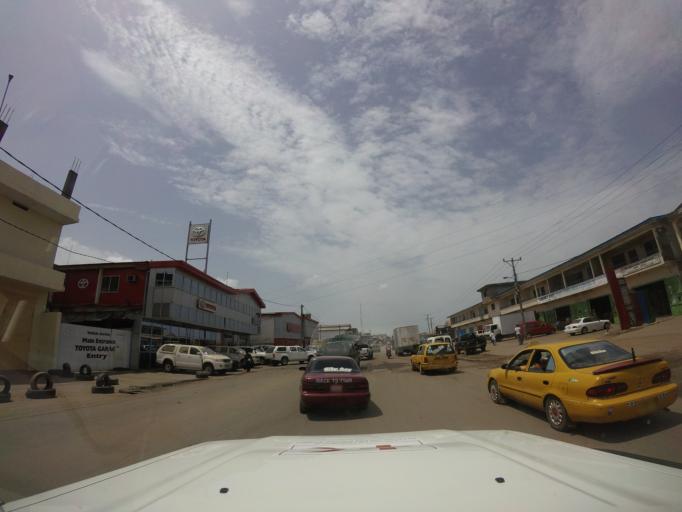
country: LR
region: Montserrado
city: Monrovia
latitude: 6.3501
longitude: -10.7873
